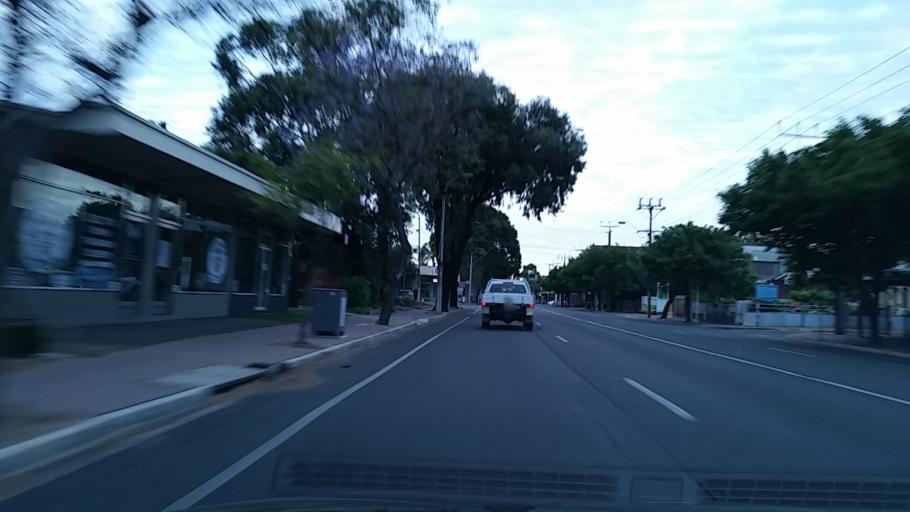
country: AU
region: South Australia
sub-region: Norwood Payneham St Peters
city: Royston Park
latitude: -34.9067
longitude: 138.6302
